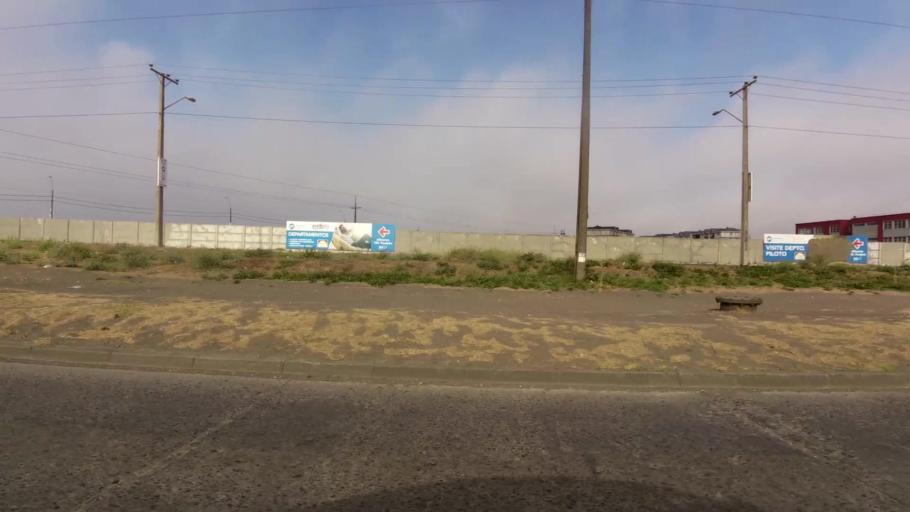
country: CL
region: Biobio
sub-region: Provincia de Concepcion
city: Concepcion
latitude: -36.7994
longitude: -73.1064
